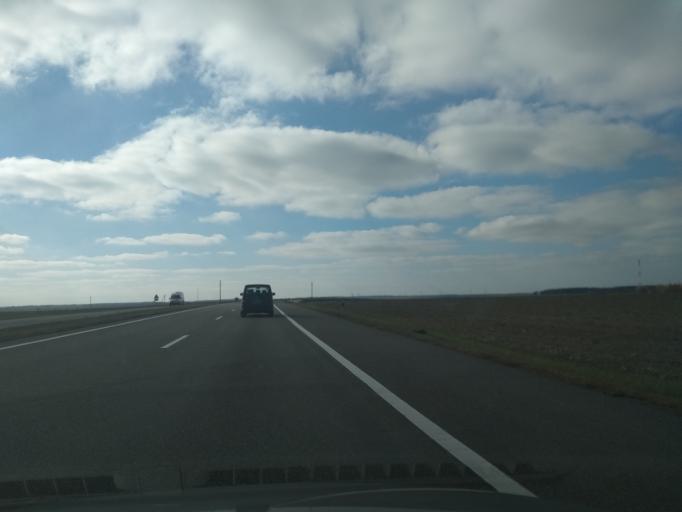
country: BY
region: Minsk
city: Haradzyeya
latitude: 53.4114
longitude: 26.5646
